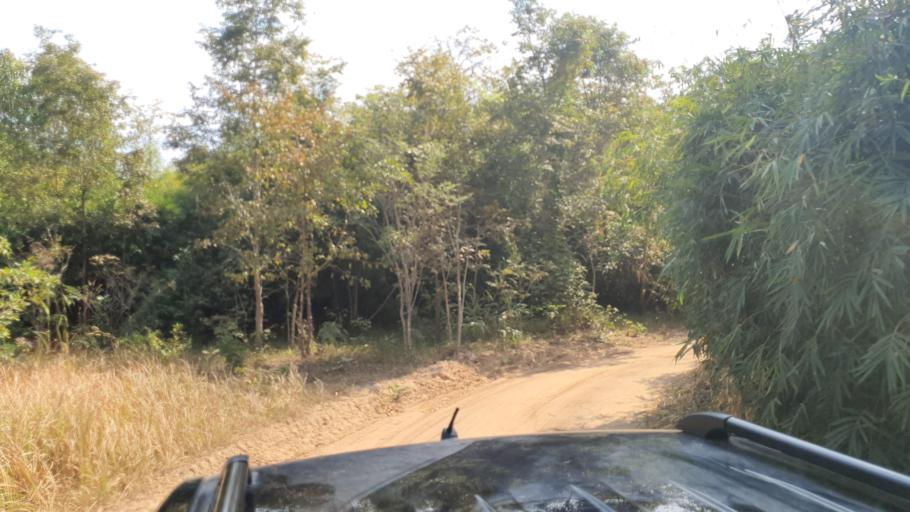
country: TH
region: Changwat Bueng Kan
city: Si Wilai
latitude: 18.2694
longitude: 103.7996
